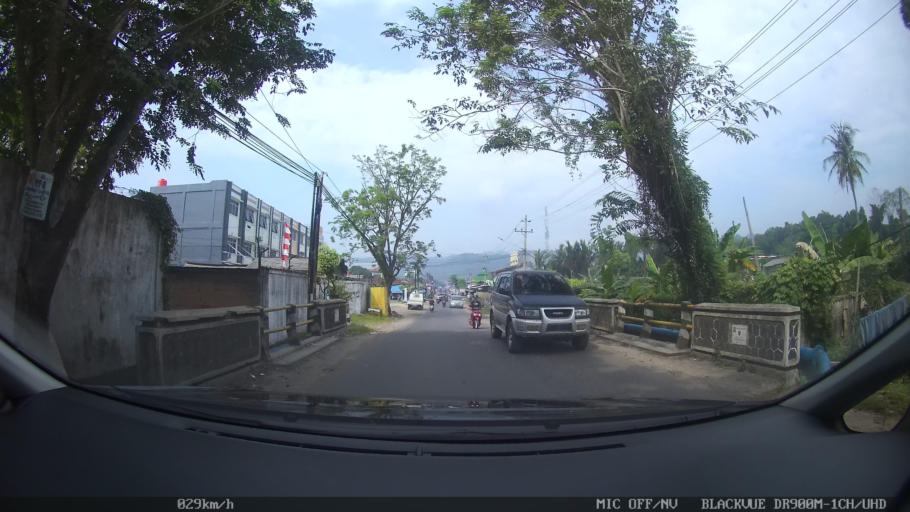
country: ID
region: Lampung
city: Bandarlampung
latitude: -5.4576
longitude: 105.2539
